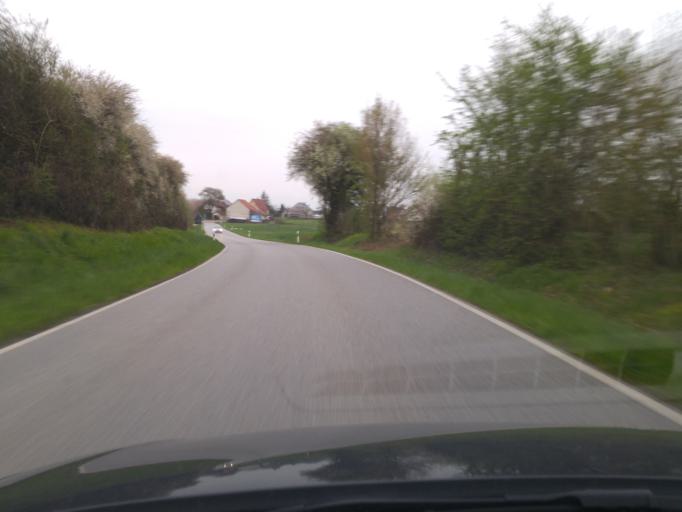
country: DE
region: Baden-Wuerttemberg
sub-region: Regierungsbezirk Stuttgart
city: Bad Rappenau
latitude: 49.2451
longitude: 9.1300
